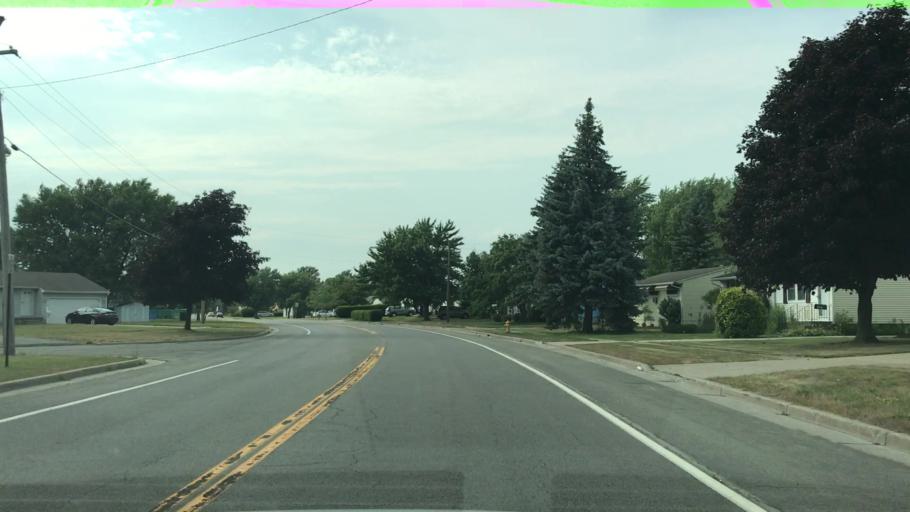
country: US
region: New York
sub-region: Erie County
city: Depew
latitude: 42.9158
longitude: -78.7100
